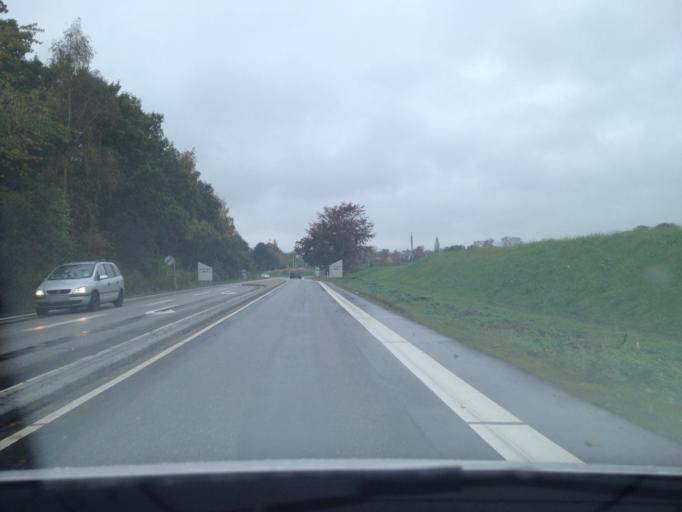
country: DK
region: Capital Region
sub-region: Fredensborg Kommune
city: Fredensborg
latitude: 55.9629
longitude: 12.4085
